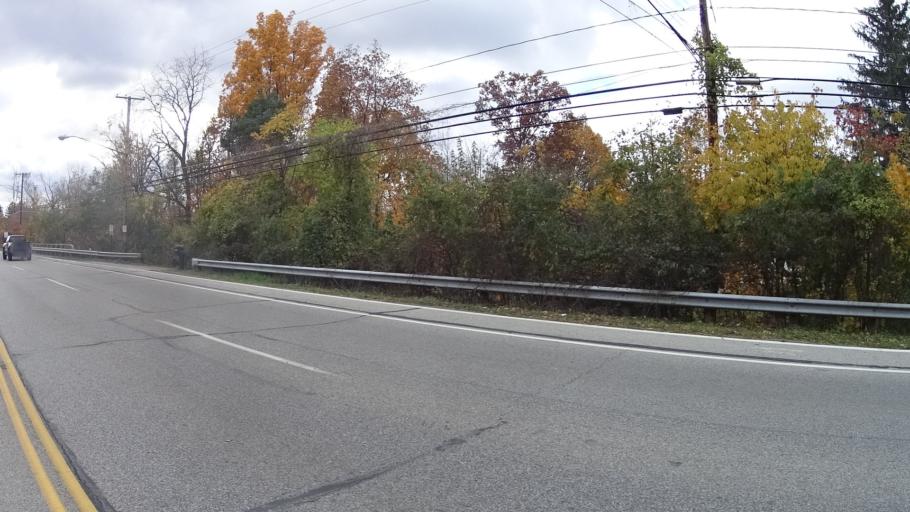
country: US
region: Ohio
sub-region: Lorain County
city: Amherst
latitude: 41.4228
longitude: -82.2088
